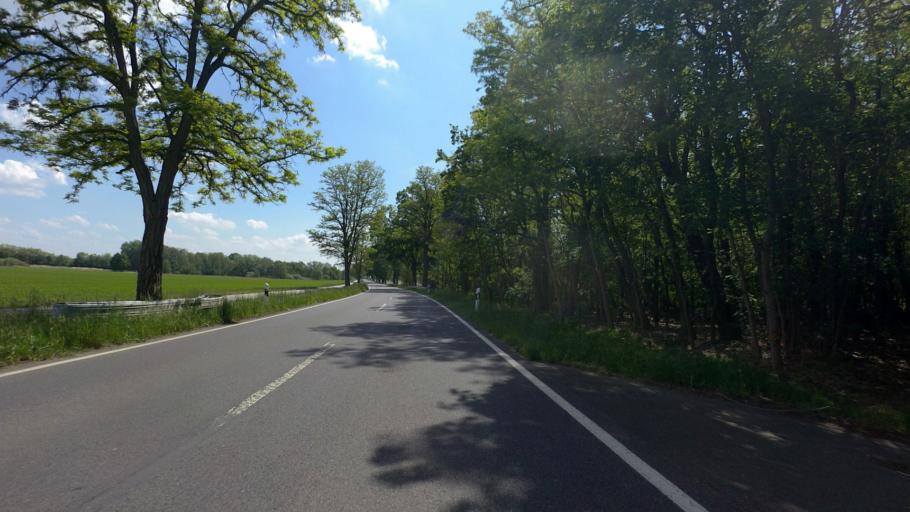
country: DE
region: Brandenburg
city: Neu Zauche
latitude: 51.9177
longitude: 14.1010
